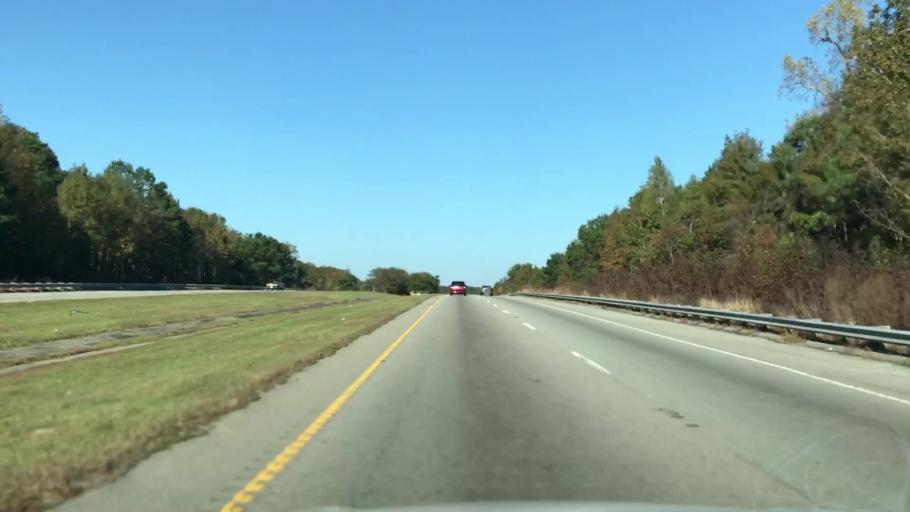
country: US
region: South Carolina
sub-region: Charleston County
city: Shell Point
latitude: 32.8223
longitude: -80.0726
